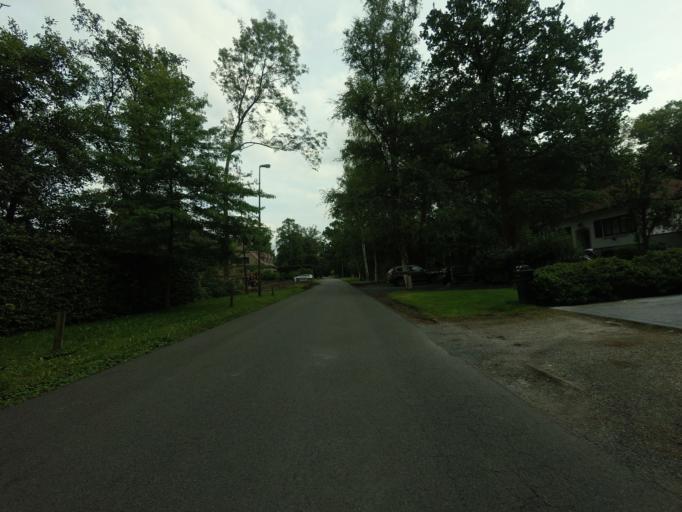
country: BE
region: Flanders
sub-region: Provincie Vlaams-Brabant
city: Kampenhout
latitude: 50.9353
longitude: 4.5601
